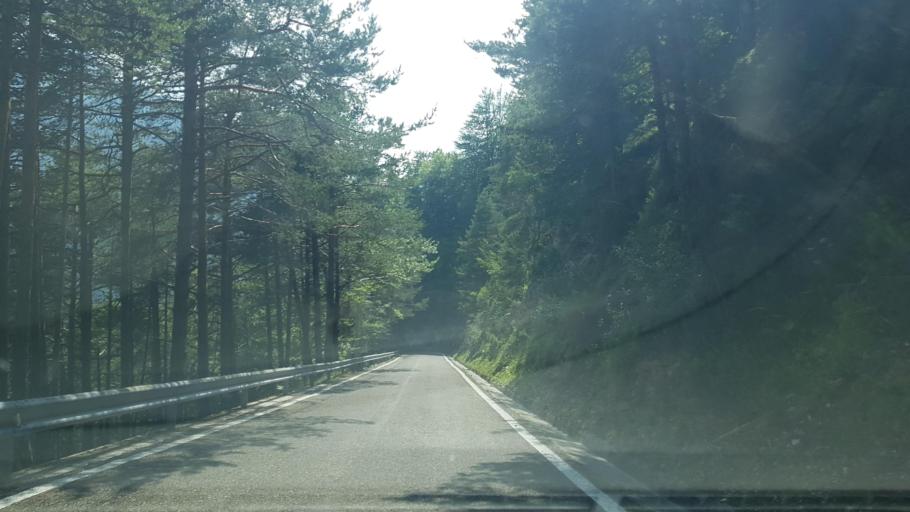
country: IT
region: Friuli Venezia Giulia
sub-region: Provincia di Udine
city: Dogna
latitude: 46.4553
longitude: 13.3770
